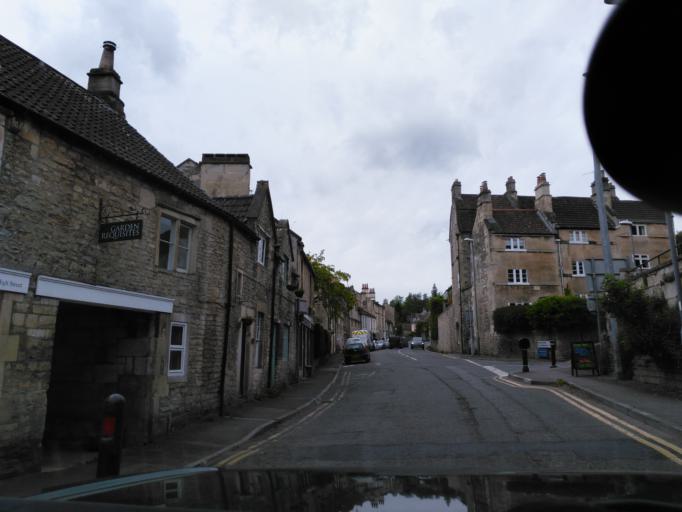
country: GB
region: England
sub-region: Bath and North East Somerset
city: Bath
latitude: 51.4058
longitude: -2.3203
